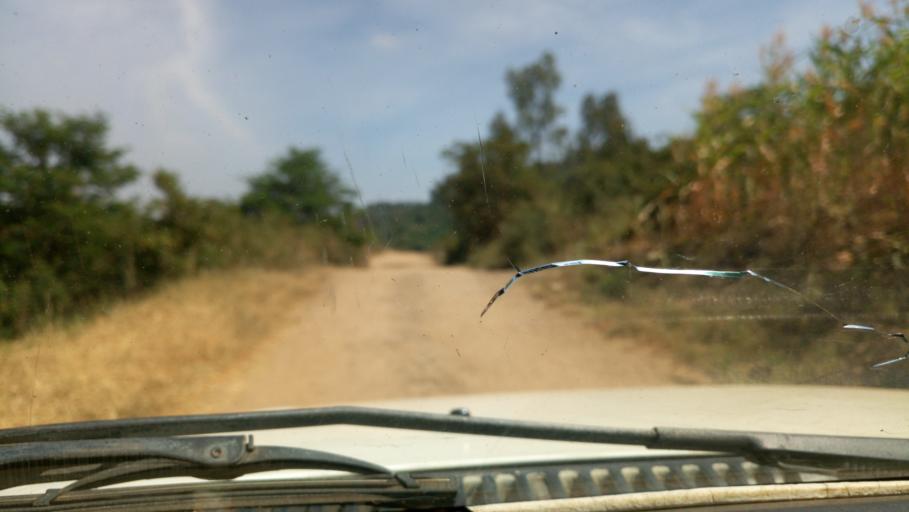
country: KE
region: Murang'a District
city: Murang'a
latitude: -0.7490
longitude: 37.1588
